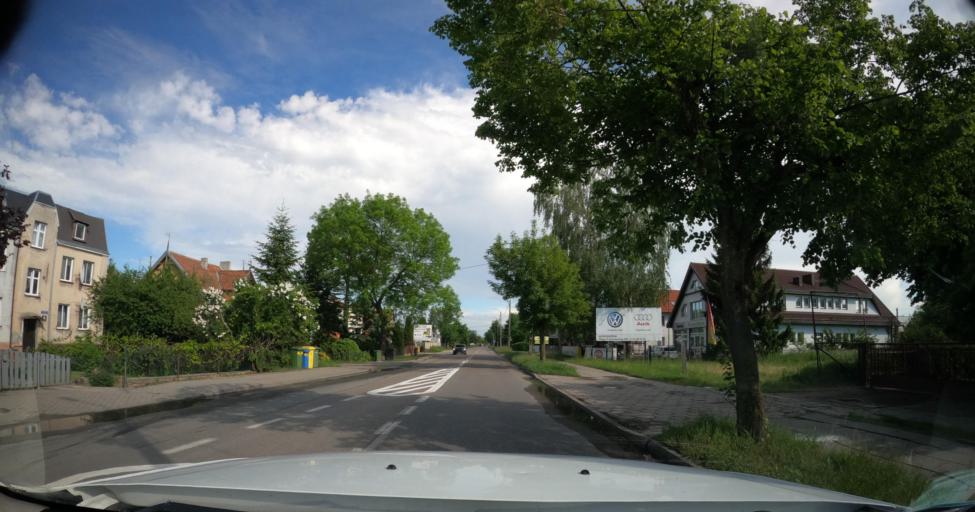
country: PL
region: Warmian-Masurian Voivodeship
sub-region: Powiat elblaski
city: Elblag
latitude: 54.1651
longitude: 19.3774
